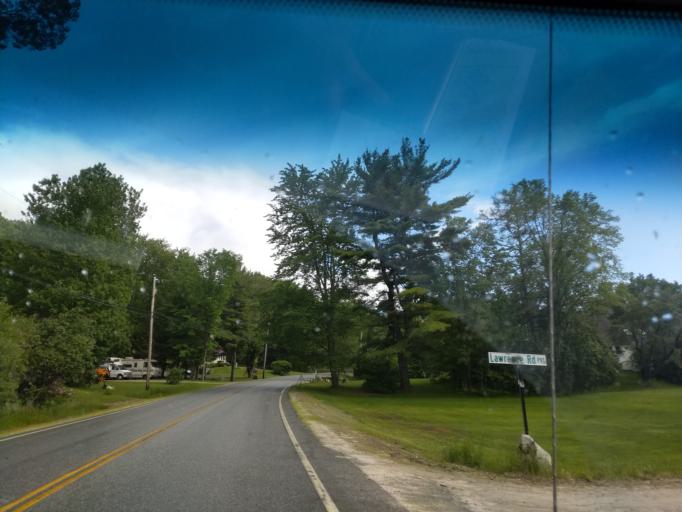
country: US
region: Maine
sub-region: Cumberland County
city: North Windham
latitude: 43.8012
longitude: -70.3679
